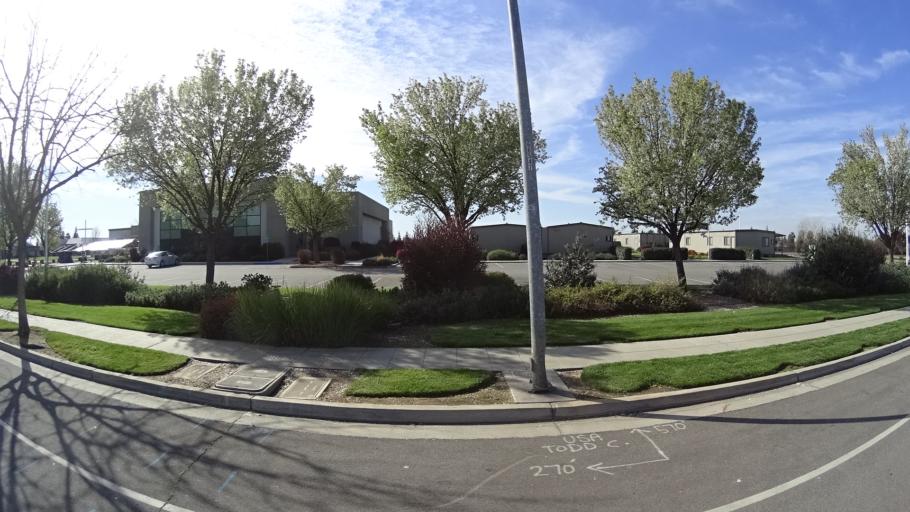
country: US
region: California
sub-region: Fresno County
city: West Park
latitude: 36.8335
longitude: -119.8769
